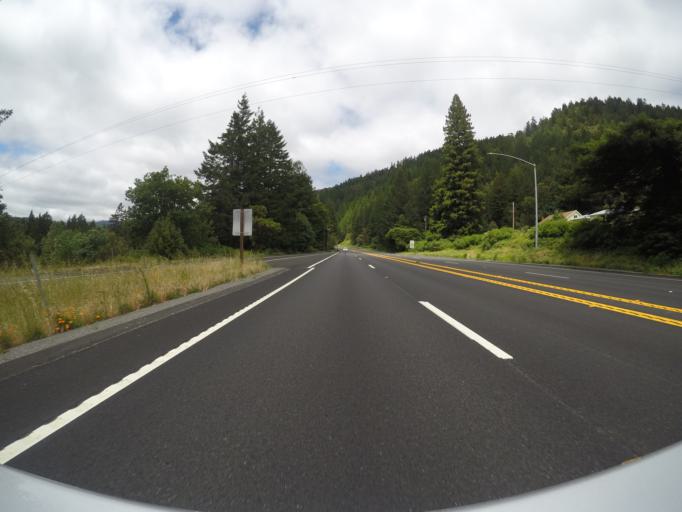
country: US
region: California
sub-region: Humboldt County
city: Redway
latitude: 40.3235
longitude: -123.9215
